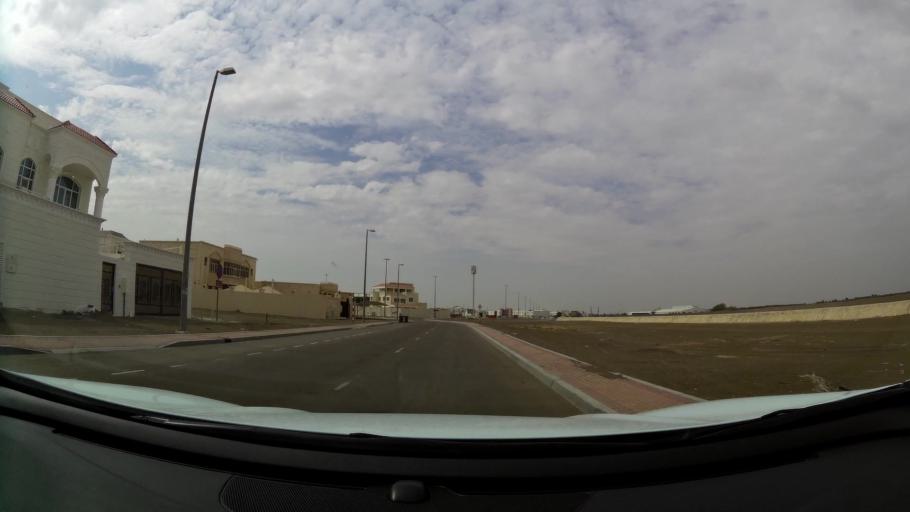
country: AE
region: Abu Dhabi
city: Al Ain
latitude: 24.1952
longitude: 55.8142
